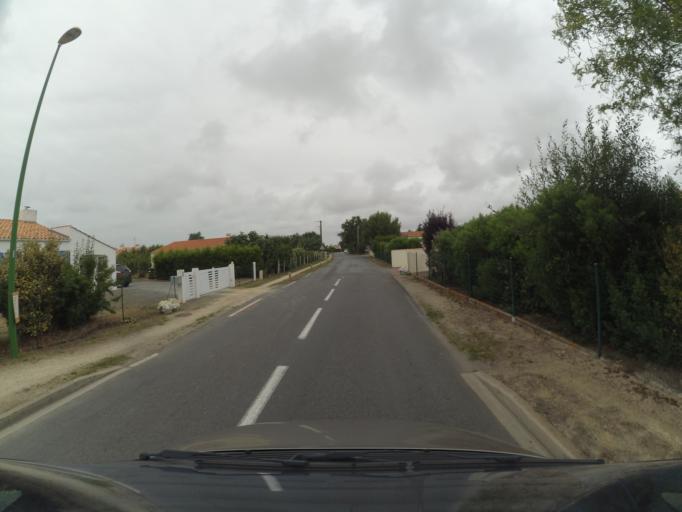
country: FR
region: Pays de la Loire
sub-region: Departement de la Vendee
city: Saint-Urbain
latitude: 46.8811
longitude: -2.0084
